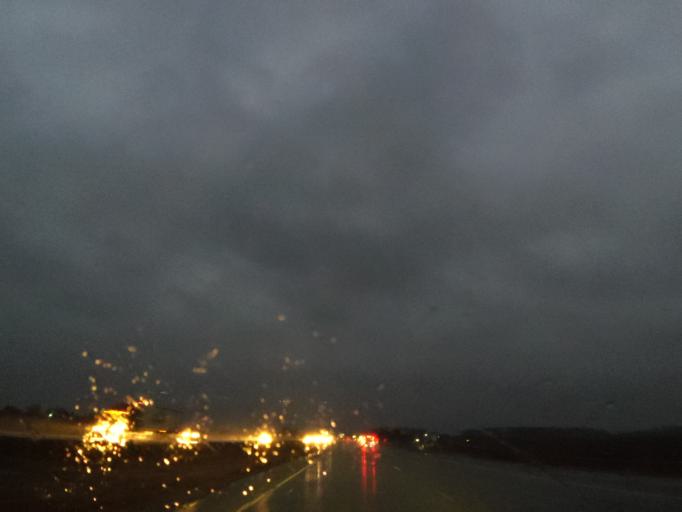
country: US
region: Minnesota
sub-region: Freeborn County
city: Albert Lea
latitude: 43.7182
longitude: -93.3198
